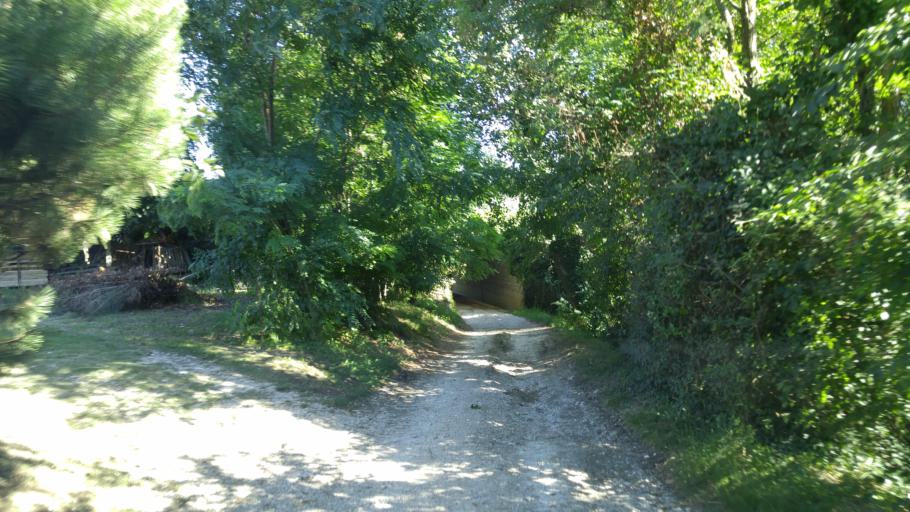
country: IT
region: The Marches
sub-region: Provincia di Pesaro e Urbino
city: Calcinelli
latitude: 43.7513
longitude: 12.9254
